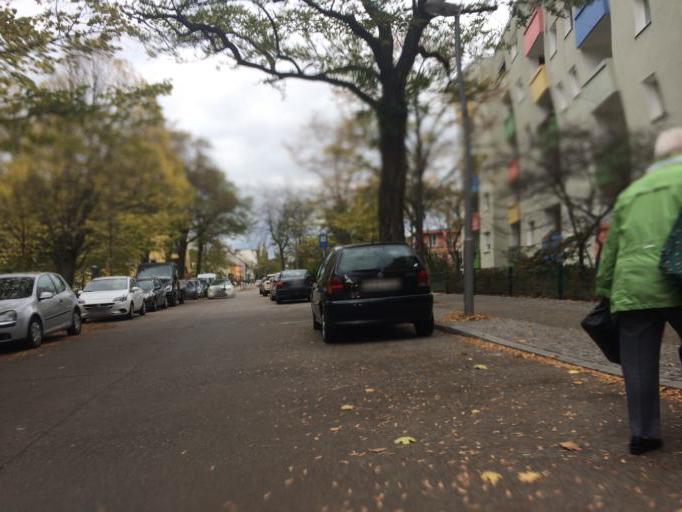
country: DE
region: Berlin
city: Reinickendorf
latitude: 52.5732
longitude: 13.3188
